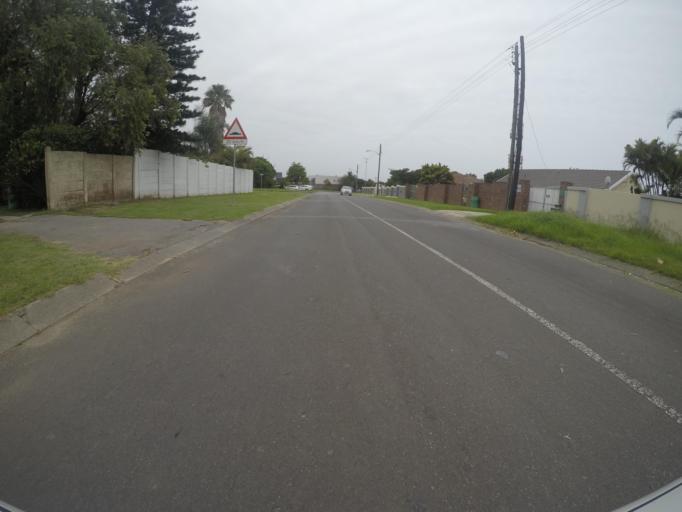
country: ZA
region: Eastern Cape
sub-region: Buffalo City Metropolitan Municipality
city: East London
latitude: -32.9694
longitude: 27.9378
